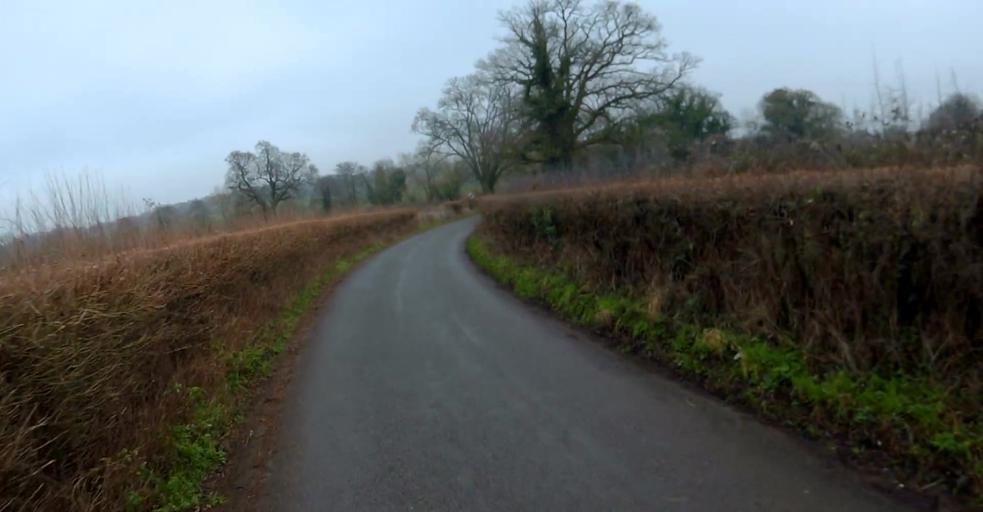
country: GB
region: England
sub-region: Hampshire
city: Hook
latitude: 51.3182
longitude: -0.9436
